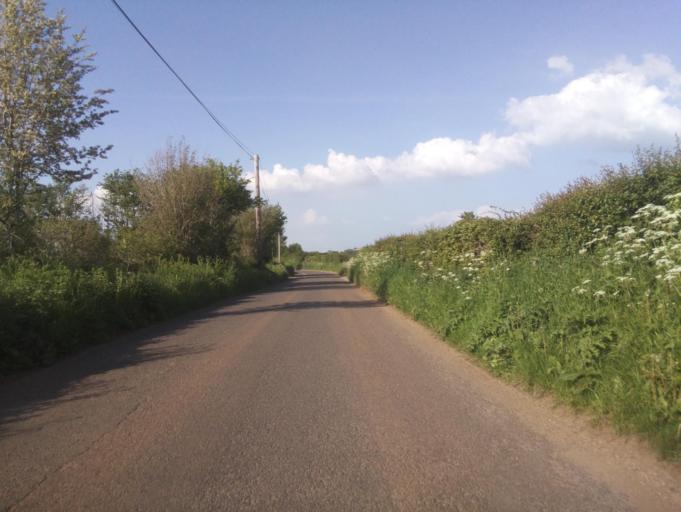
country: GB
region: England
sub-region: Wiltshire
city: Biddestone
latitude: 51.4792
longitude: -2.1748
